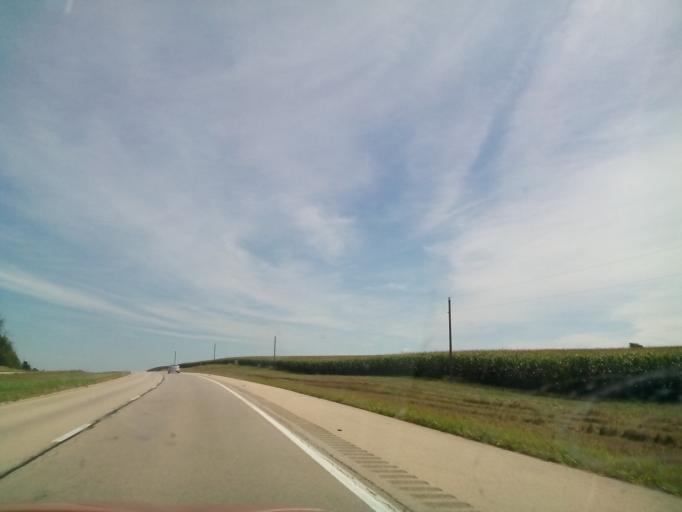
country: US
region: Illinois
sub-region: Winnebago County
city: Pecatonica
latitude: 42.2757
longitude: -89.4350
